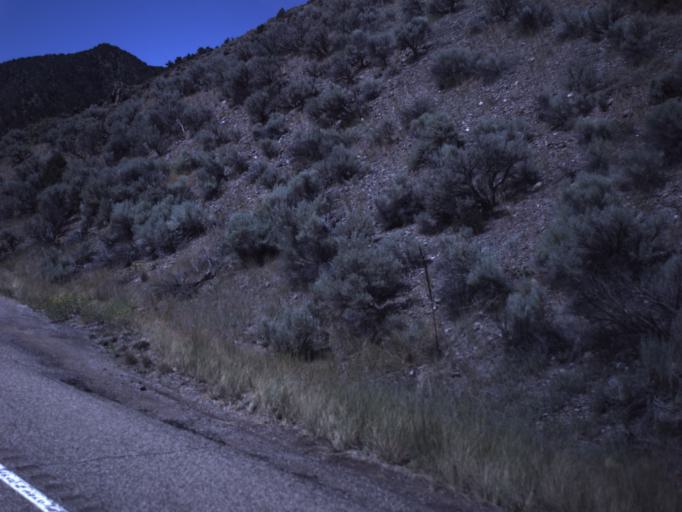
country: US
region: Utah
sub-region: Piute County
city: Junction
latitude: 38.0969
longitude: -112.3367
